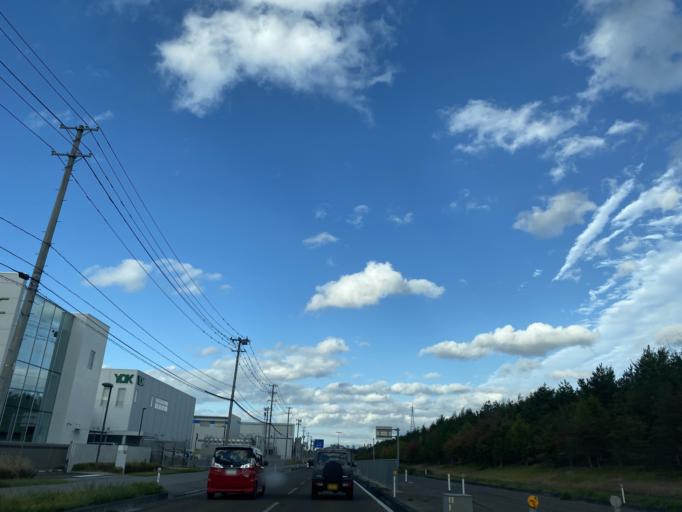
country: JP
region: Miyagi
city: Tomiya
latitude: 38.3657
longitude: 140.8523
